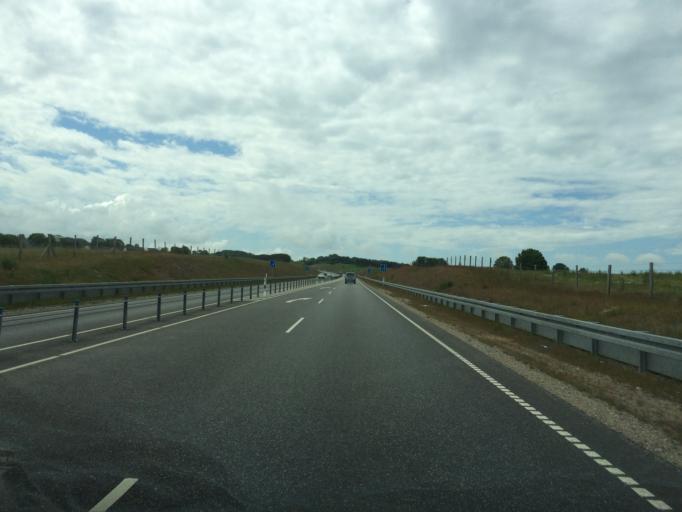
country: DK
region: Zealand
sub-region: Odsherred Kommune
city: Hojby
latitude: 55.8314
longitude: 11.5931
